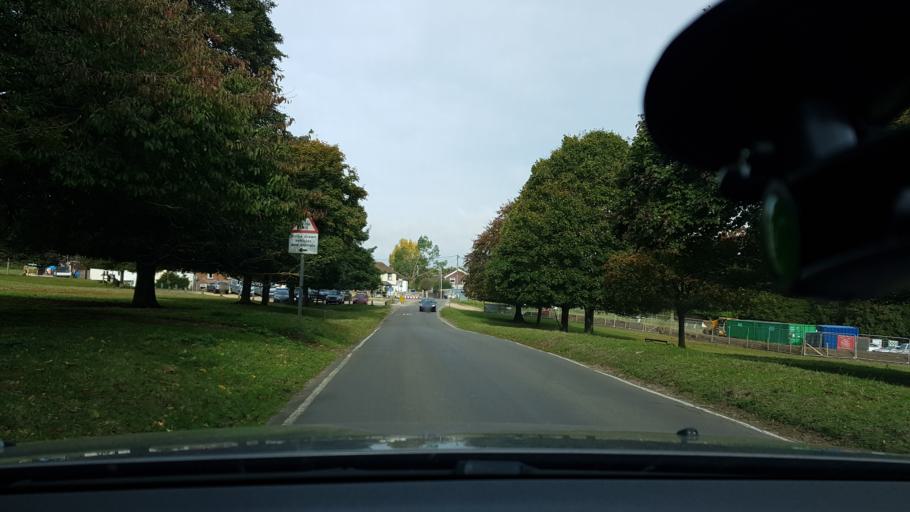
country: GB
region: England
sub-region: West Berkshire
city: Hungerford
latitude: 51.4122
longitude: -1.5083
